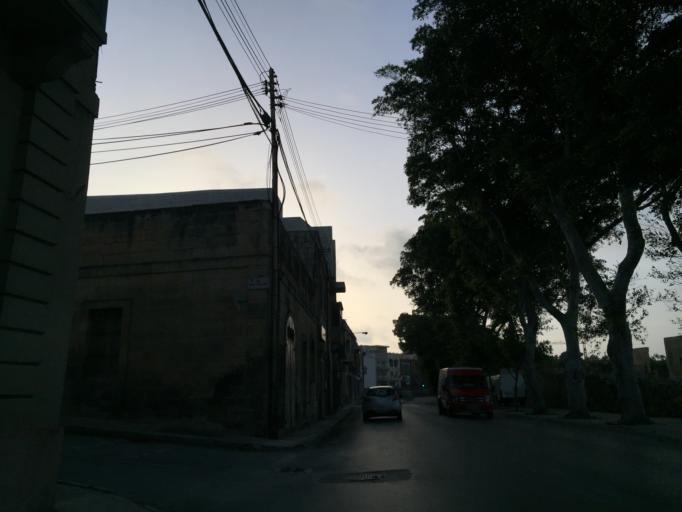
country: MT
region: Saint Paul's Bay
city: San Pawl il-Bahar
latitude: 35.9366
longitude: 14.4130
